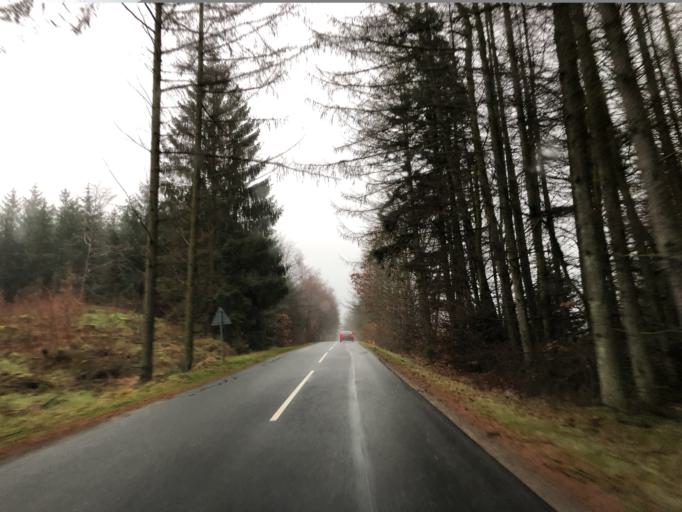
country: DK
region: Central Jutland
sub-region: Holstebro Kommune
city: Ulfborg
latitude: 56.2068
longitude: 8.4042
